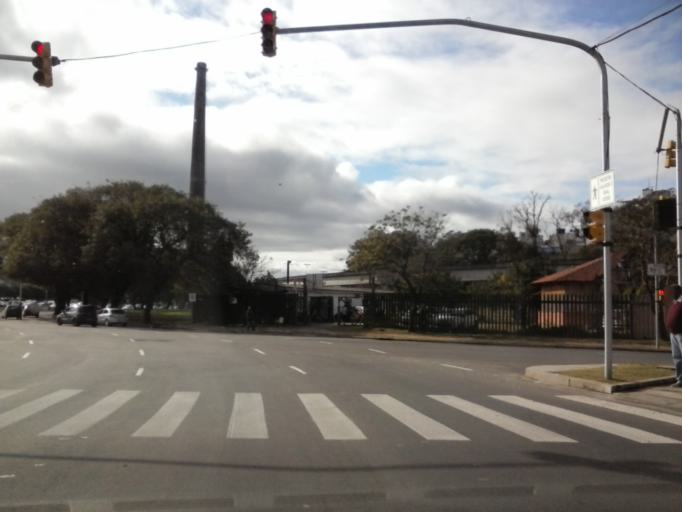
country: BR
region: Rio Grande do Sul
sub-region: Porto Alegre
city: Porto Alegre
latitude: -30.0368
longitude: -51.2406
